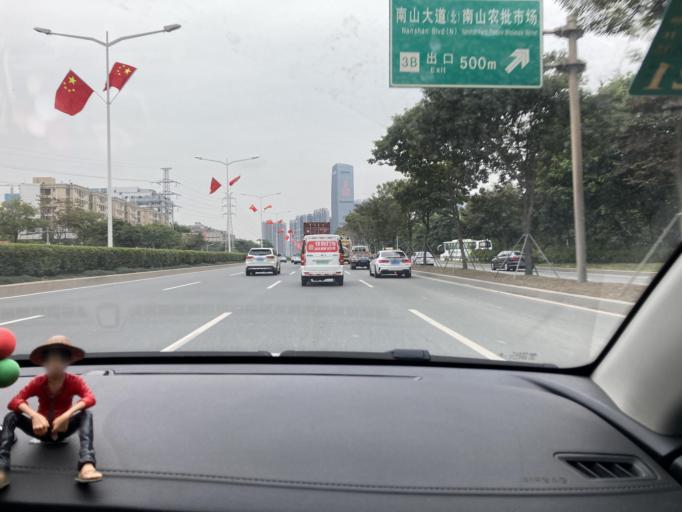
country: CN
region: Guangdong
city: Xin'an
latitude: 22.5554
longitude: 113.9273
